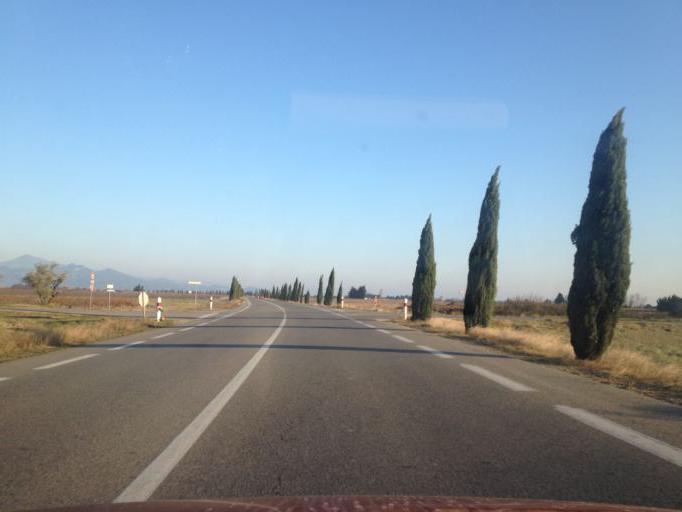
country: FR
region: Provence-Alpes-Cote d'Azur
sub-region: Departement du Vaucluse
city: Camaret-sur-Aigues
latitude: 44.1539
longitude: 4.8710
